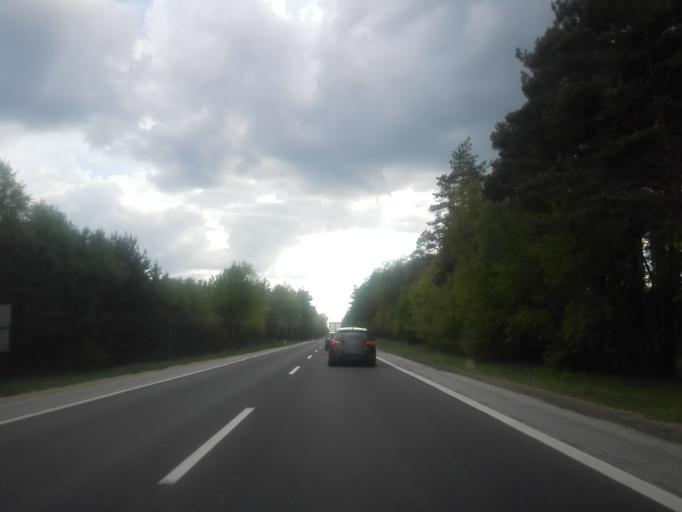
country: PL
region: Masovian Voivodeship
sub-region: Powiat ostrowski
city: Brok
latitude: 52.7675
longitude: 21.8196
